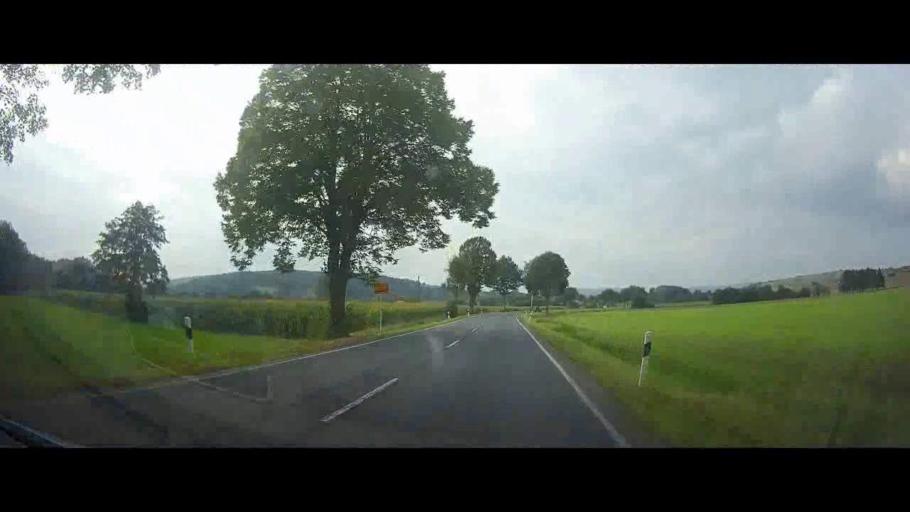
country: DE
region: Lower Saxony
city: Adelebsen
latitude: 51.5893
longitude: 9.6851
